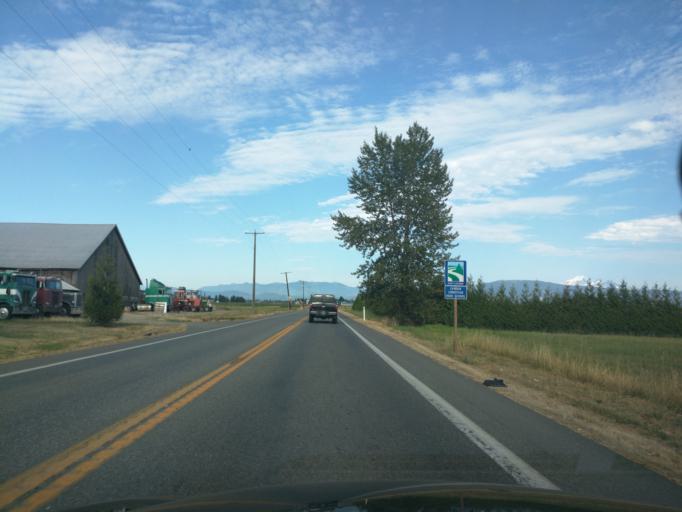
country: US
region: Washington
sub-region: Whatcom County
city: Lynden
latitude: 48.9642
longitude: -122.4829
